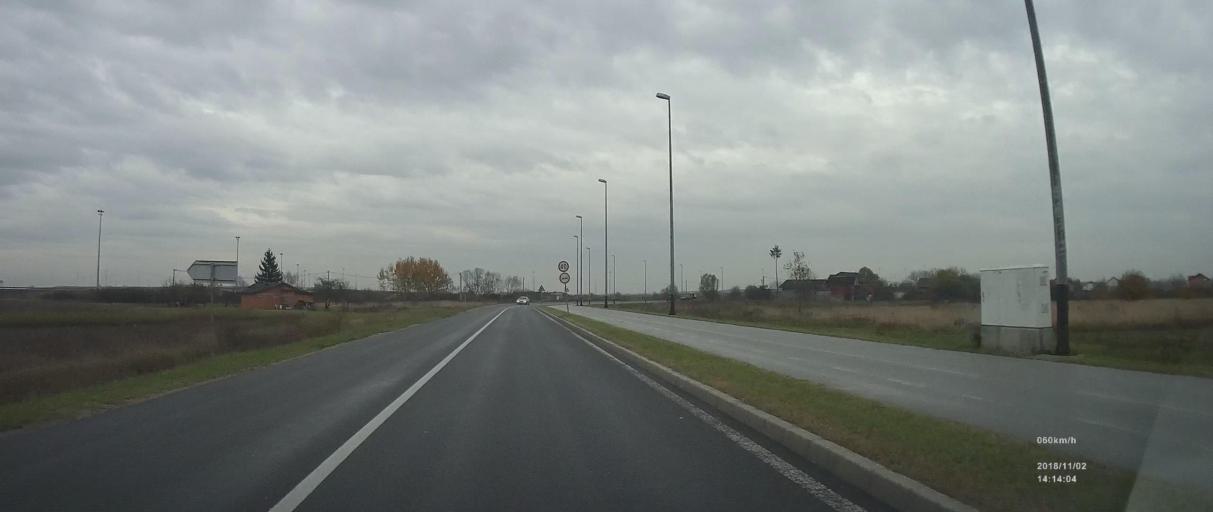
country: HR
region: Zagrebacka
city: Gradici
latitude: 45.6939
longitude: 16.0607
